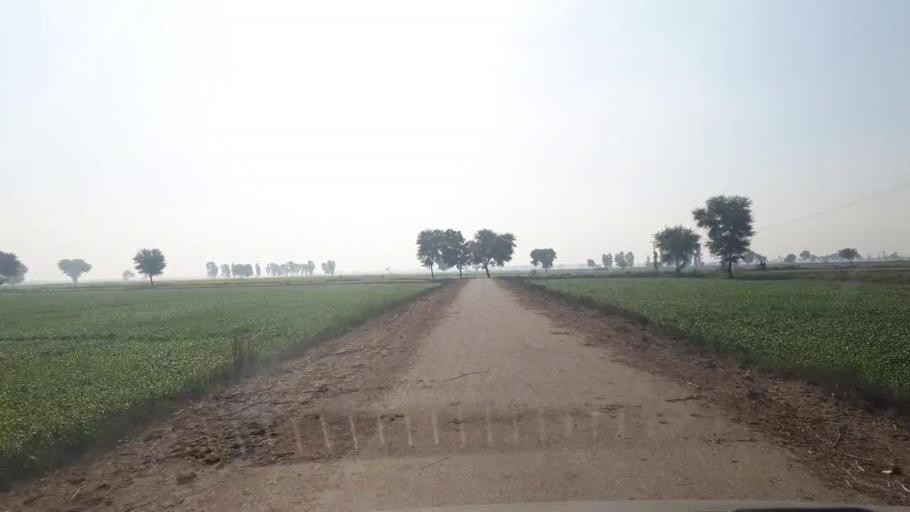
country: PK
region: Sindh
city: Shahdadpur
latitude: 25.9635
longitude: 68.5875
